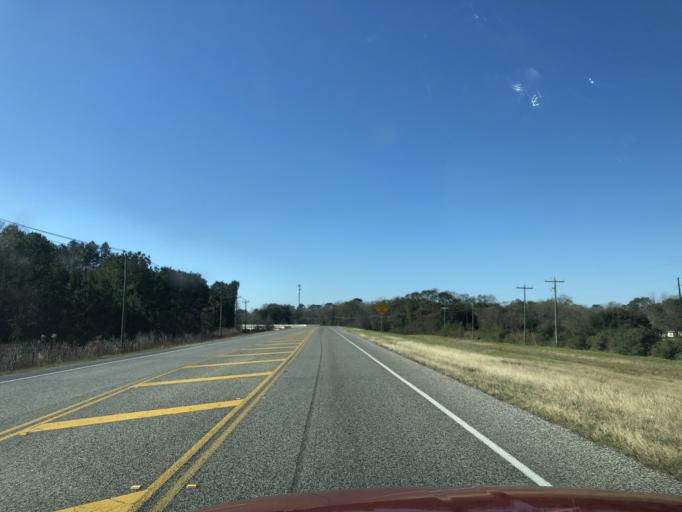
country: US
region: Texas
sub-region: Montgomery County
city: Porter Heights
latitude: 30.2172
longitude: -95.2723
